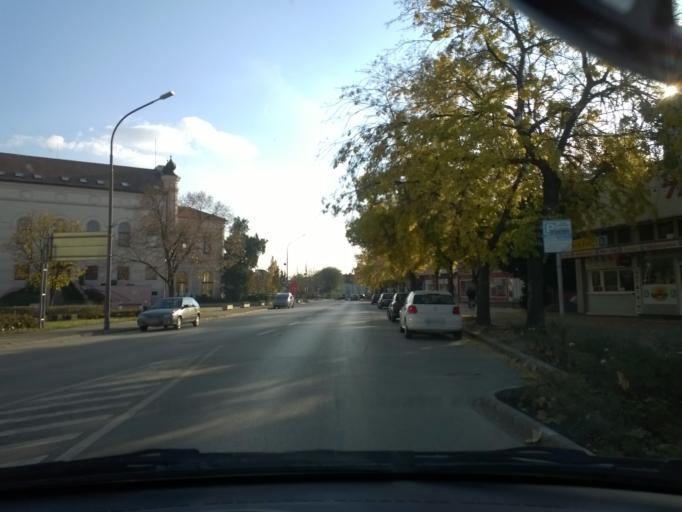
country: HU
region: Csongrad
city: Szentes
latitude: 46.6533
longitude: 20.2666
